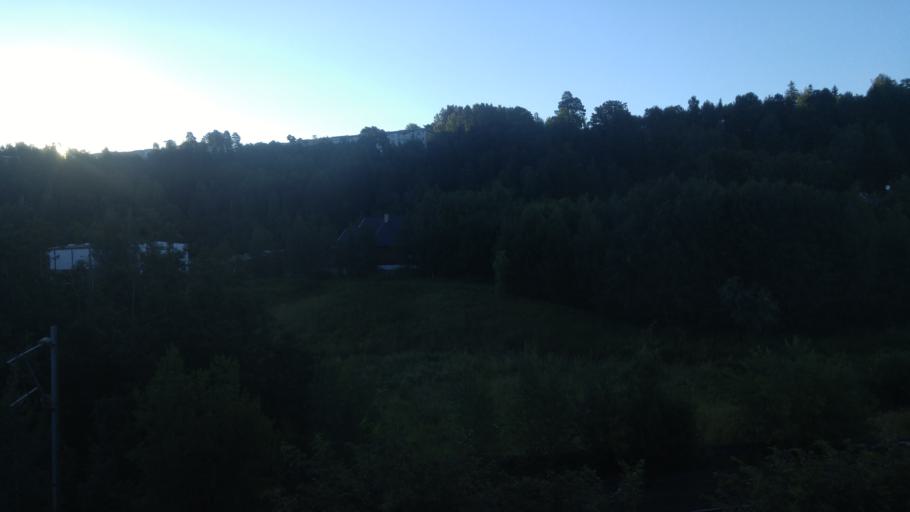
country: NO
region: Oslo
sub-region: Oslo
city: Oslo
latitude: 59.9150
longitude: 10.8283
